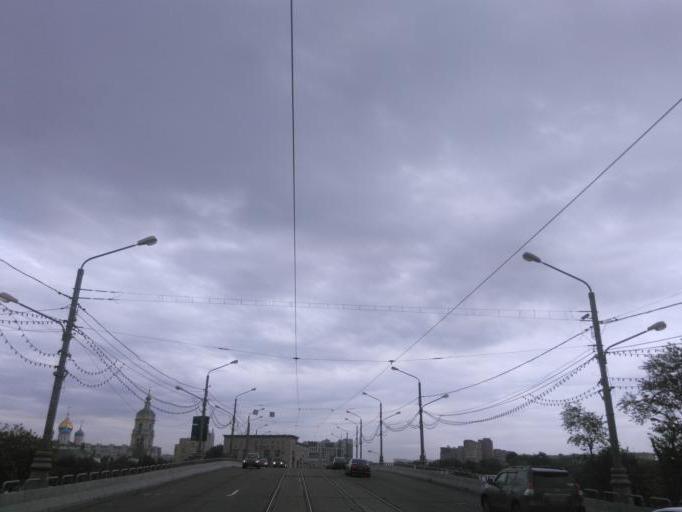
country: RU
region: Moscow
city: Taganskiy
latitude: 55.7278
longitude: 37.6517
